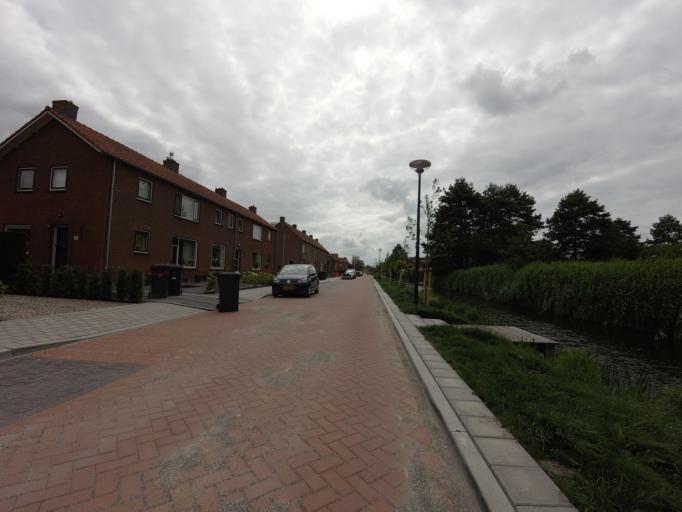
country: NL
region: Utrecht
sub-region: Stichtse Vecht
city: Breukelen
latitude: 52.1496
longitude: 4.9571
